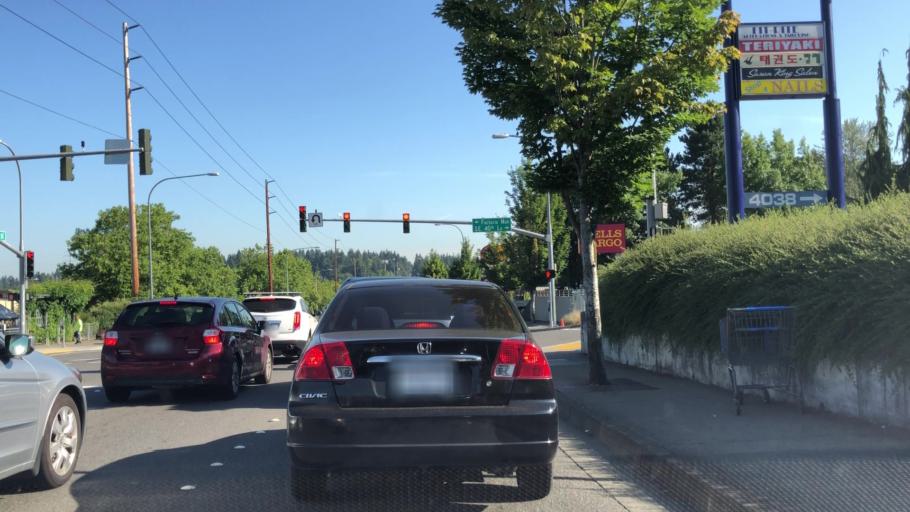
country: US
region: Washington
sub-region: King County
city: Newport
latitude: 47.5736
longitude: -122.1694
